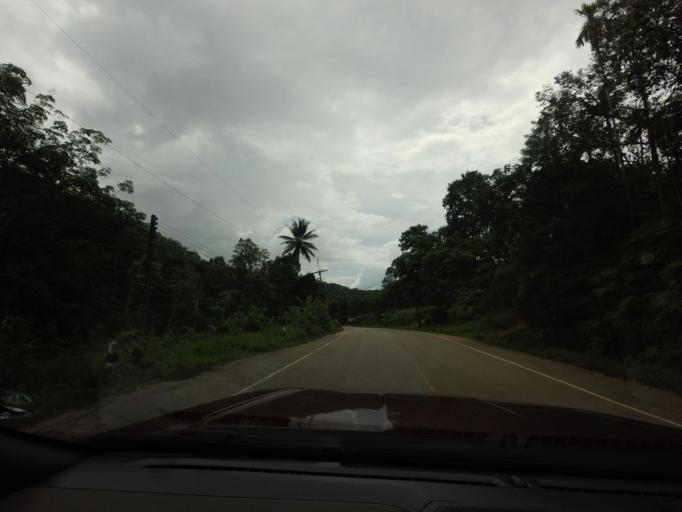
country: TH
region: Narathiwat
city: Sukhirin
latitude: 5.9832
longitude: 101.6894
